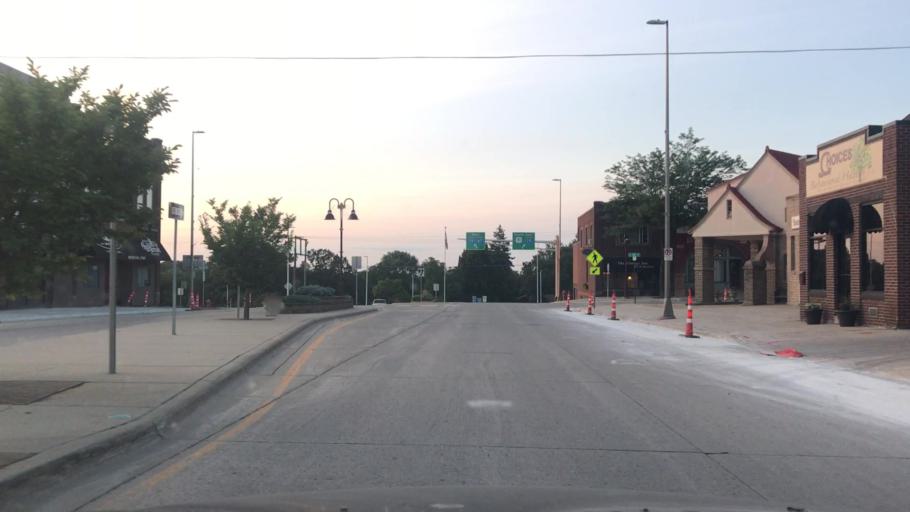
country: US
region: Minnesota
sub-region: Redwood County
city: Redwood Falls
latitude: 44.5399
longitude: -95.1194
